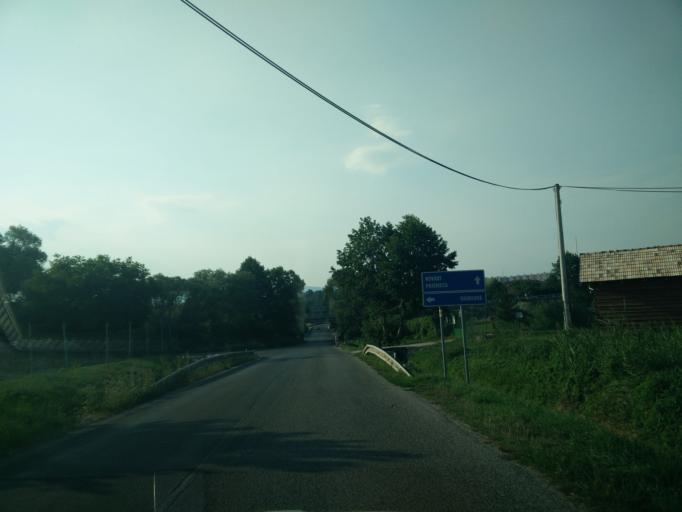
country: SK
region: Nitriansky
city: Prievidza
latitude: 48.7664
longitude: 18.6495
